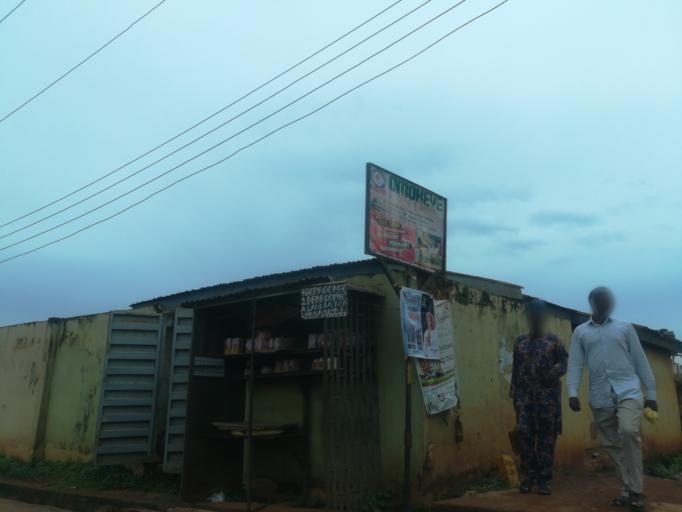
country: NG
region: Oyo
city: Egbeda
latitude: 7.3953
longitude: 3.9878
